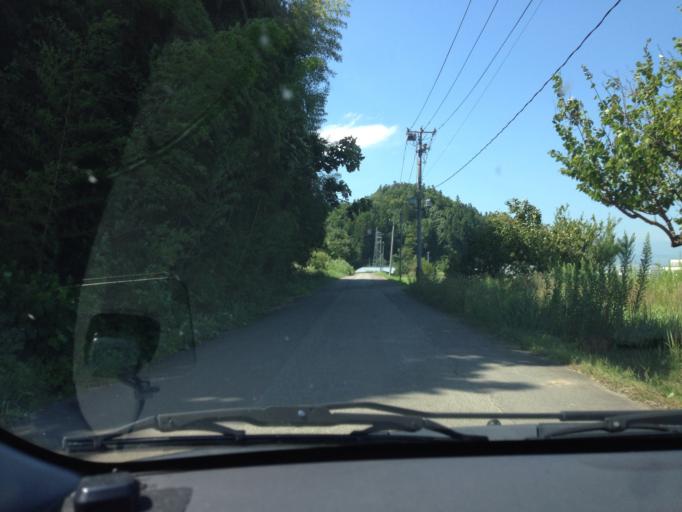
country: JP
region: Fukushima
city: Kitakata
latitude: 37.4310
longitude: 139.8810
